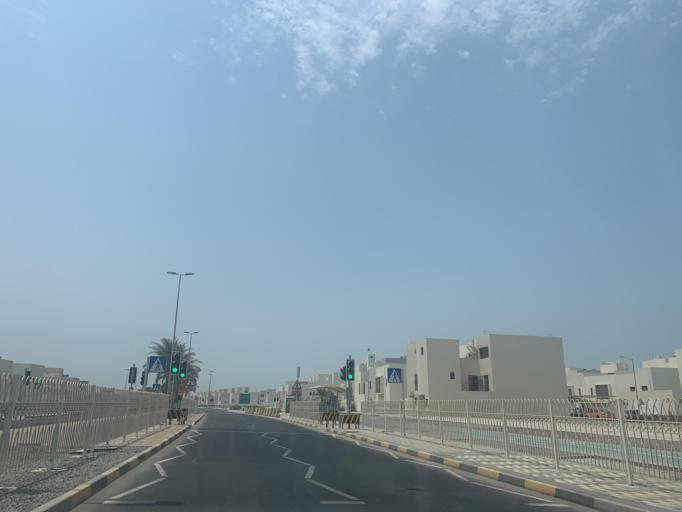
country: BH
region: Muharraq
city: Al Hadd
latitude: 26.2334
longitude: 50.6694
